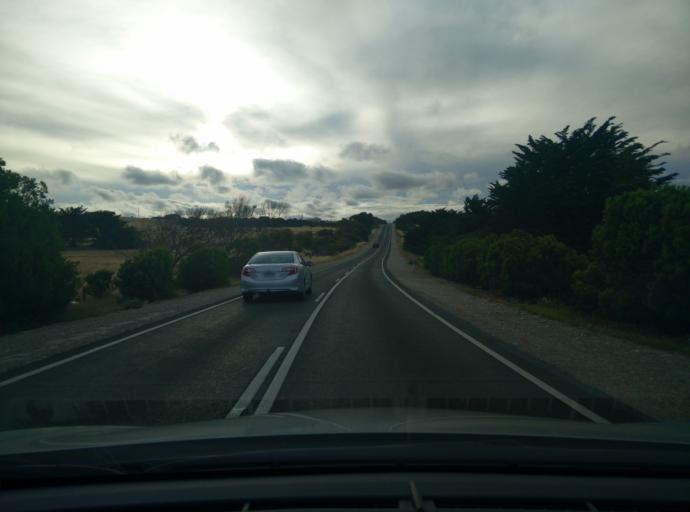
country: AU
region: South Australia
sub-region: Kangaroo Island
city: Kingscote
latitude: -35.8356
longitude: 137.7999
